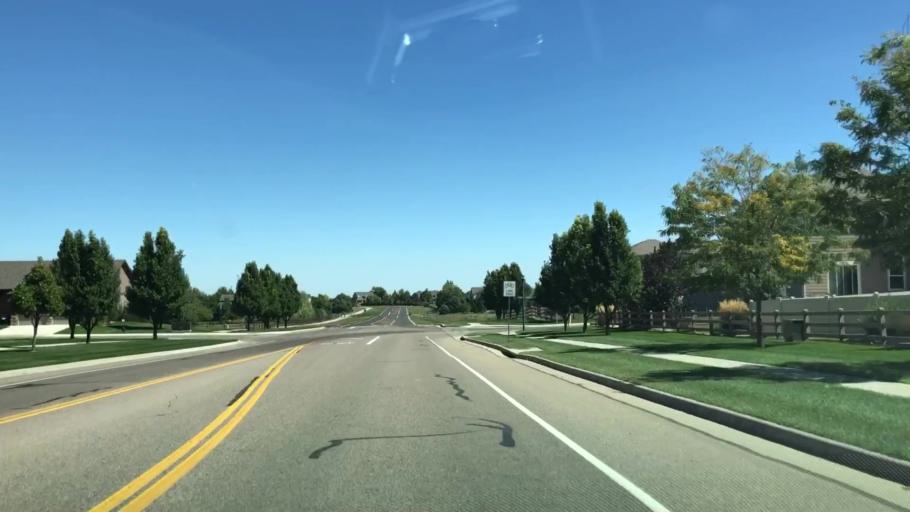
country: US
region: Colorado
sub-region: Weld County
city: Windsor
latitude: 40.4421
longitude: -104.9649
